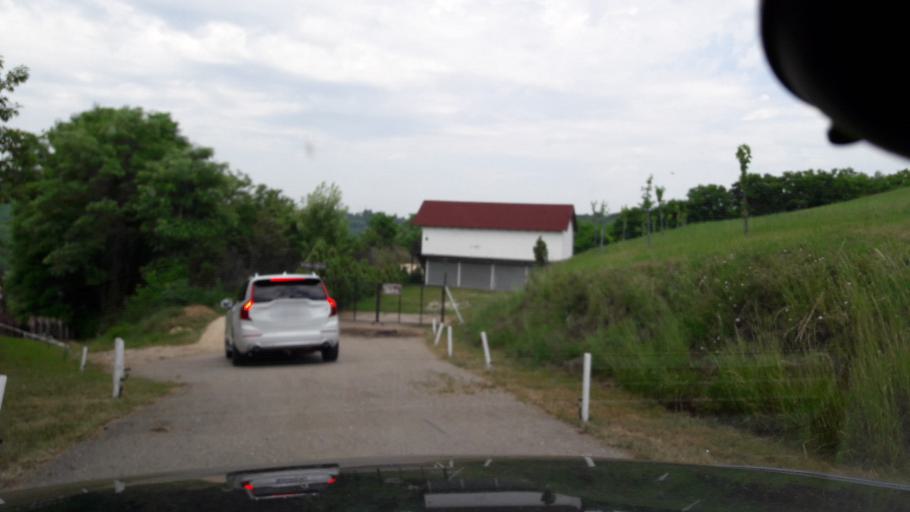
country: RS
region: Central Serbia
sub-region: Belgrade
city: Sopot
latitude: 44.6006
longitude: 20.5996
